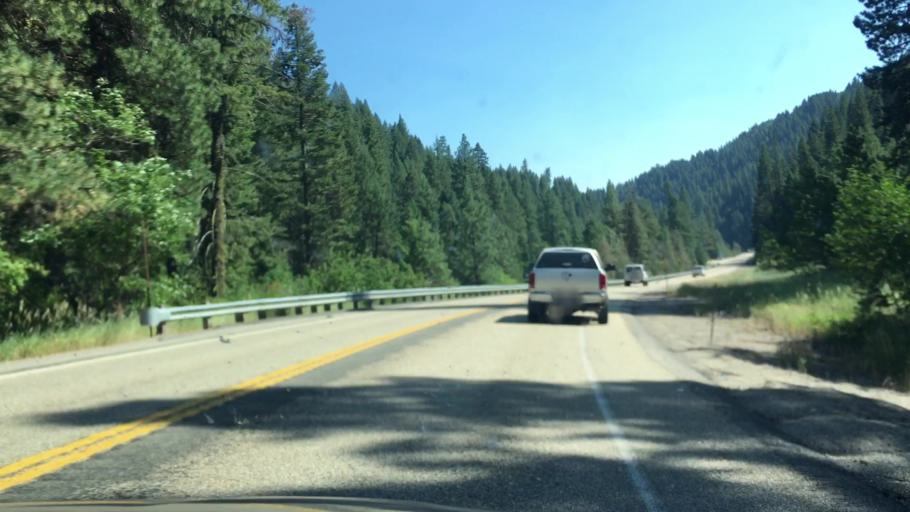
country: US
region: Idaho
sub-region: Valley County
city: Cascade
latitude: 44.1643
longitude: -116.1182
